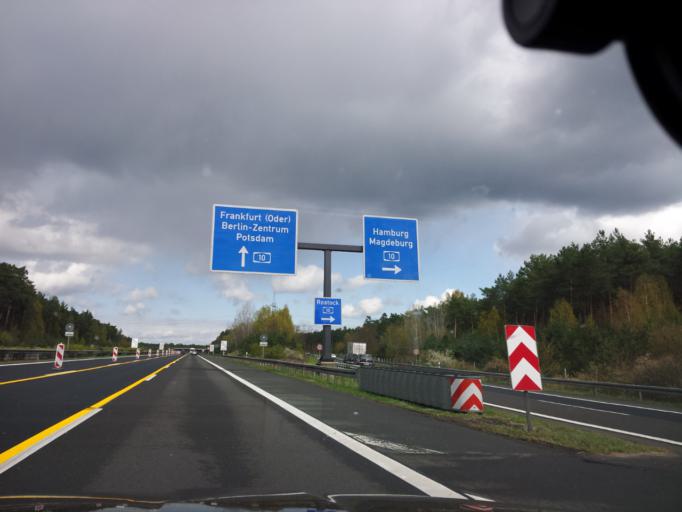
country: DE
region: Brandenburg
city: Fichtenwalde
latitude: 52.2821
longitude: 12.9137
